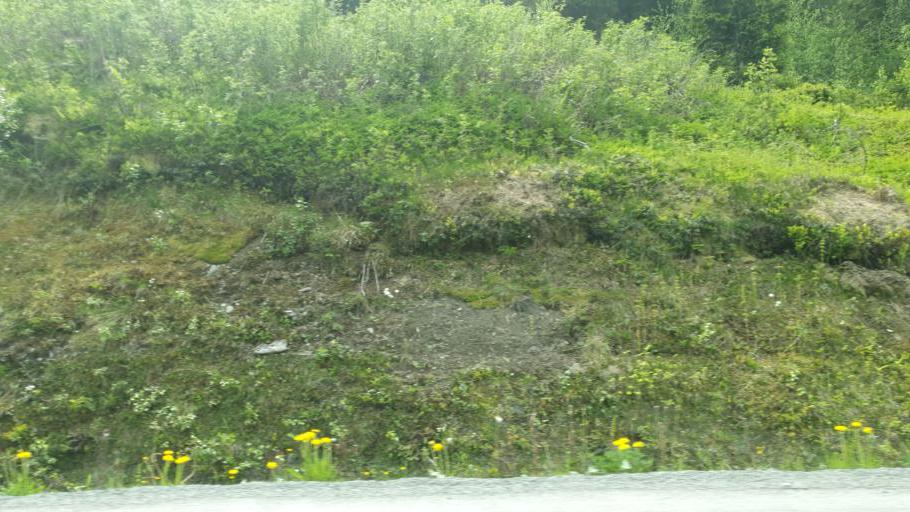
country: NO
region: Nord-Trondelag
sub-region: Leksvik
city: Leksvik
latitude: 63.6907
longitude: 10.5189
